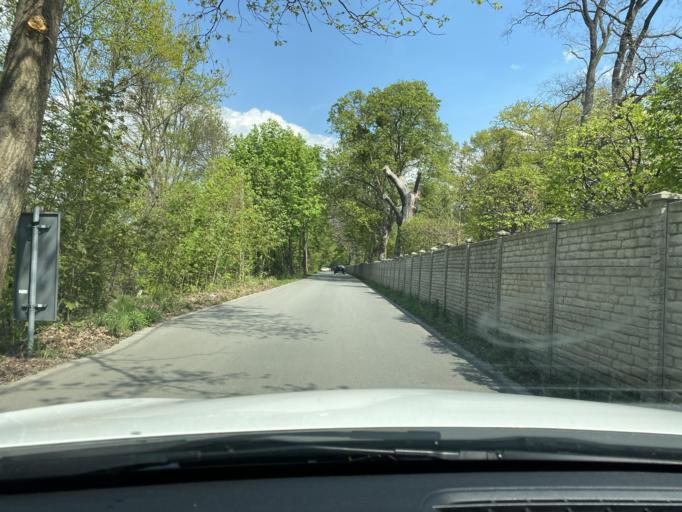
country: PL
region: Lower Silesian Voivodeship
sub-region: Powiat wroclawski
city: Wroclaw
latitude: 51.1377
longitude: 17.0056
